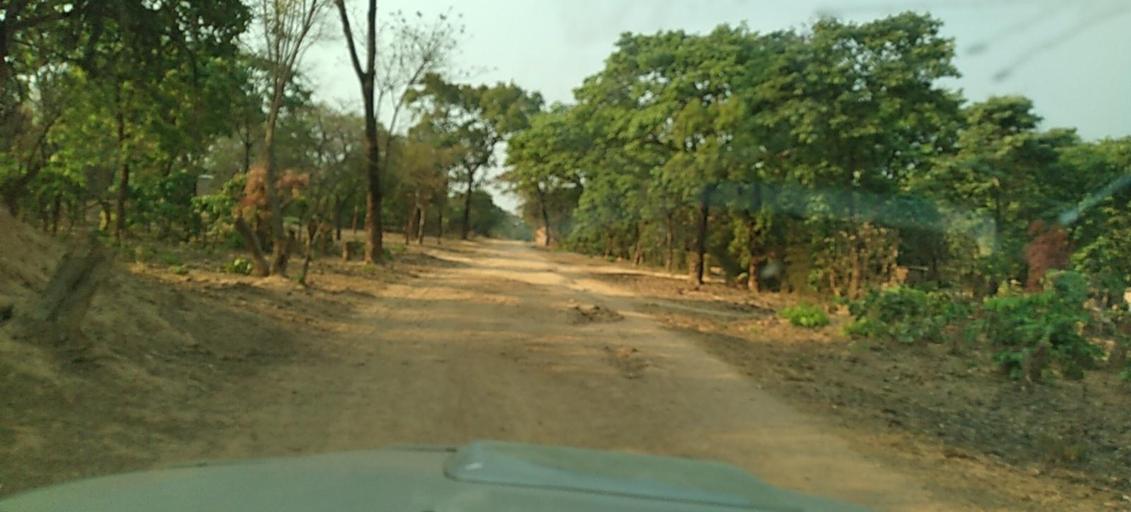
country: ZM
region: North-Western
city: Kasempa
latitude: -13.2774
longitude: 26.5556
